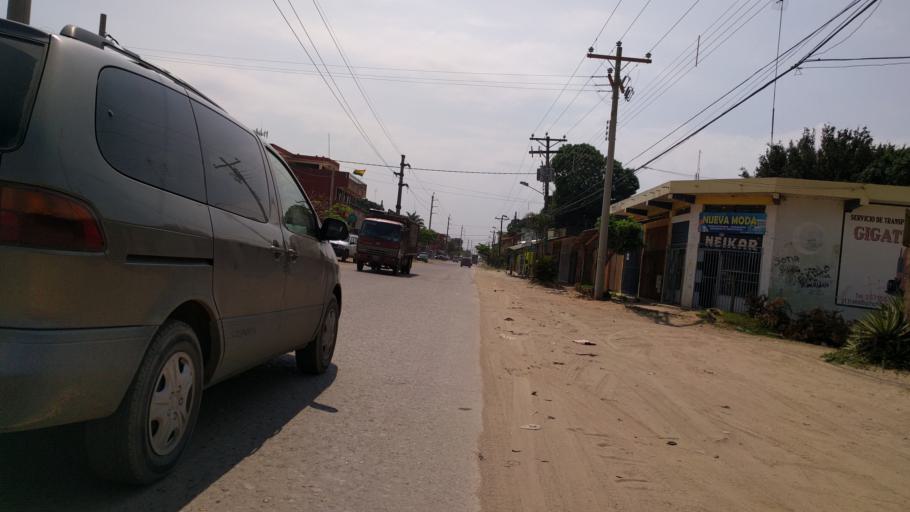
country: BO
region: Santa Cruz
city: Santa Cruz de la Sierra
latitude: -17.8495
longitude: -63.2179
